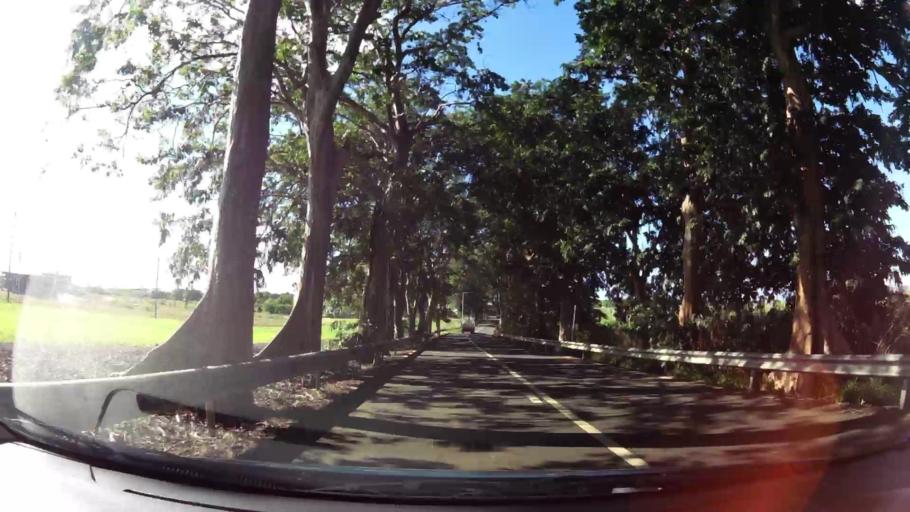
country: MU
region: Grand Port
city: Mahebourg
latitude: -20.4083
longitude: 57.6904
